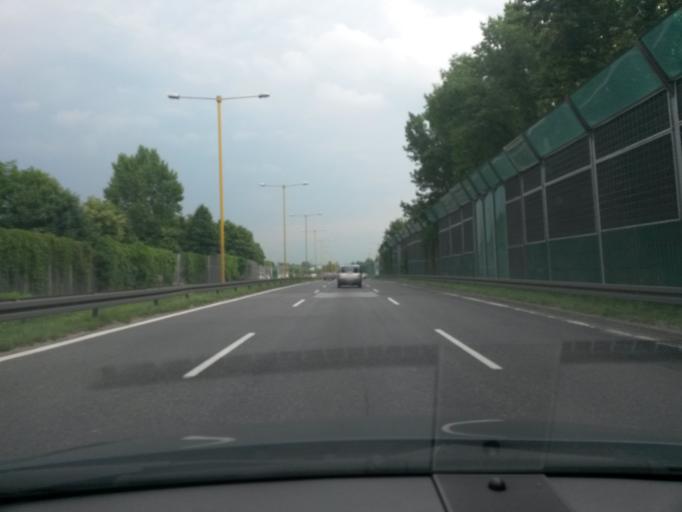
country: PL
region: Silesian Voivodeship
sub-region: Czestochowa
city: Czestochowa
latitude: 50.7741
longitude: 19.1540
